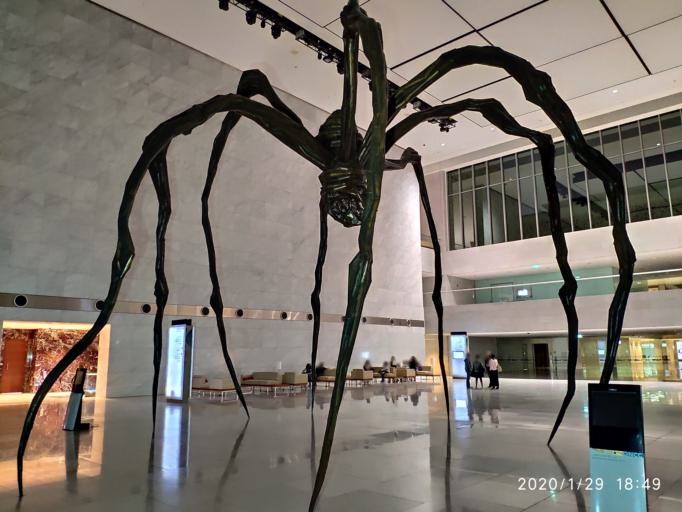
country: QA
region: Baladiyat ar Rayyan
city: Ar Rayyan
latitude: 25.3215
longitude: 51.4373
